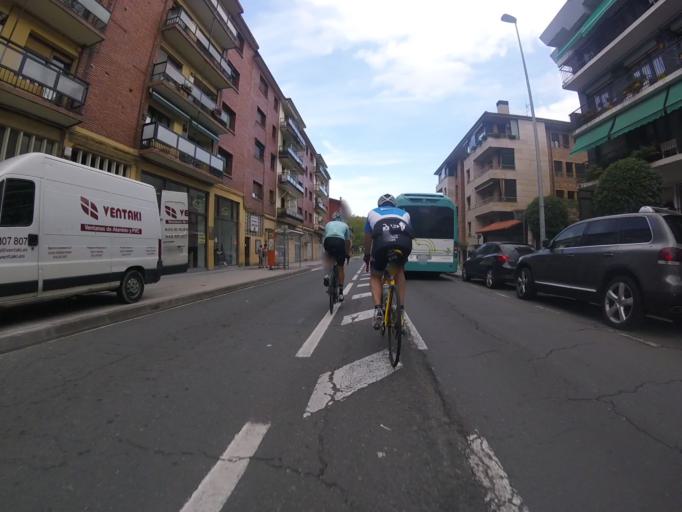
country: ES
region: Basque Country
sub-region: Provincia de Guipuzcoa
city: Villabona
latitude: 43.1897
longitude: -2.0528
